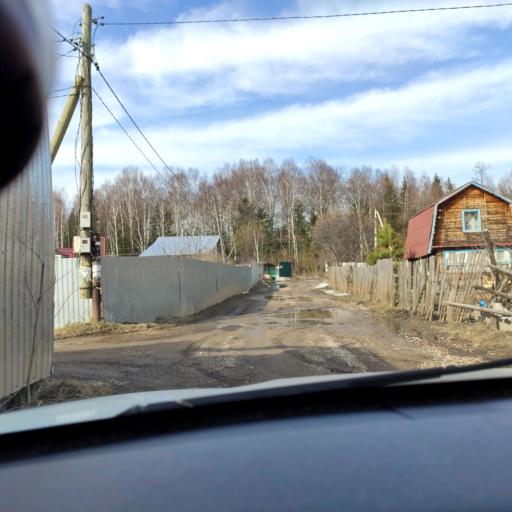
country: RU
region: Perm
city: Overyata
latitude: 58.0591
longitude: 55.9866
